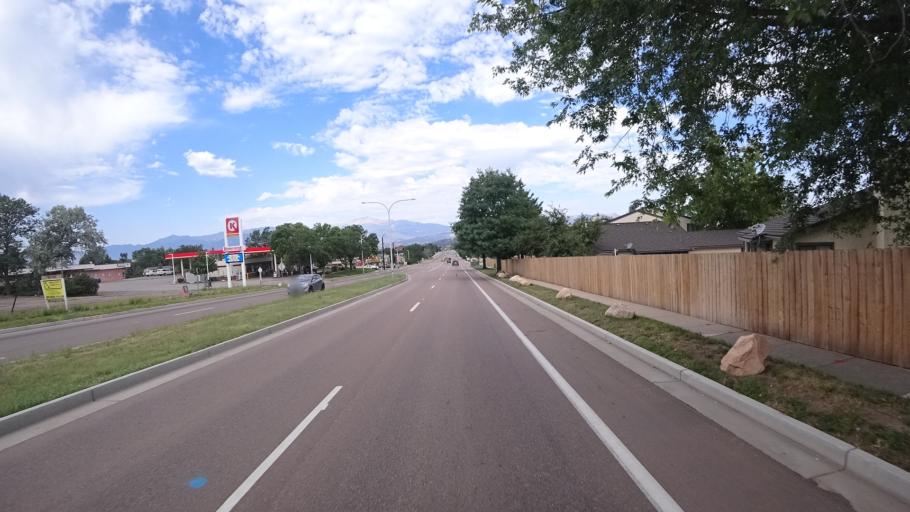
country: US
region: Colorado
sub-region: El Paso County
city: Cimarron Hills
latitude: 38.8970
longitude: -104.7369
